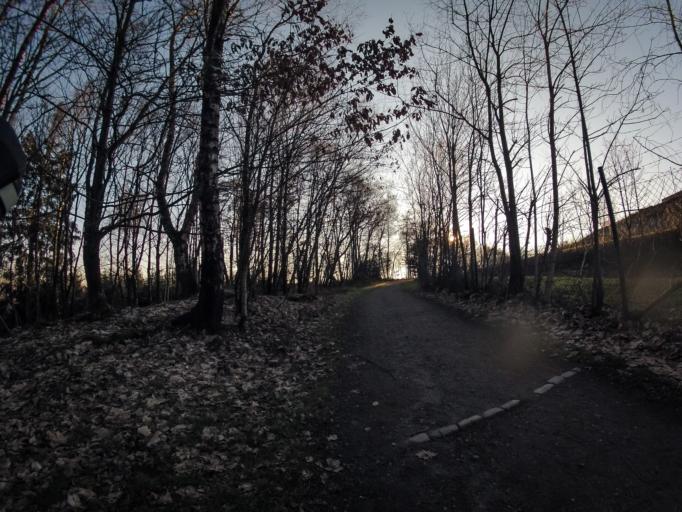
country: DE
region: Lower Saxony
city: Wallenhorst
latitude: 52.3165
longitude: 8.0298
